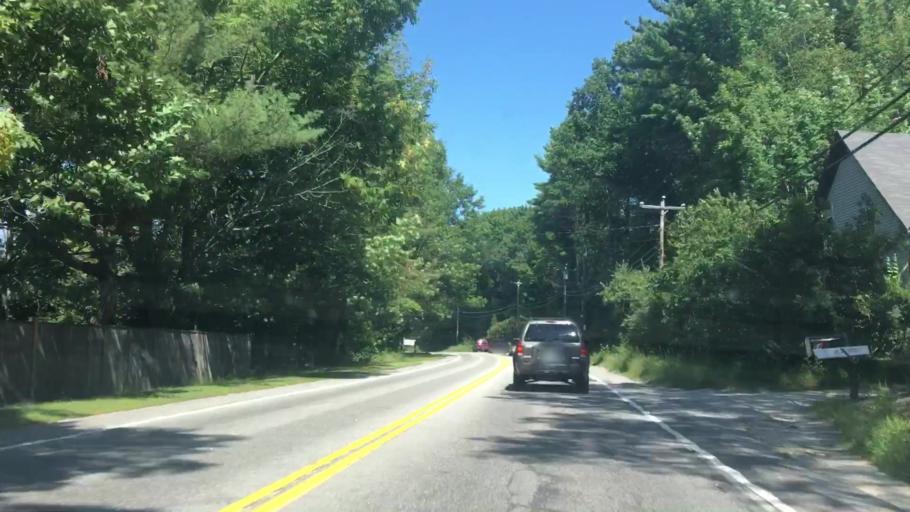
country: US
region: Maine
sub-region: Cumberland County
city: New Gloucester
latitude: 43.9018
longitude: -70.3247
